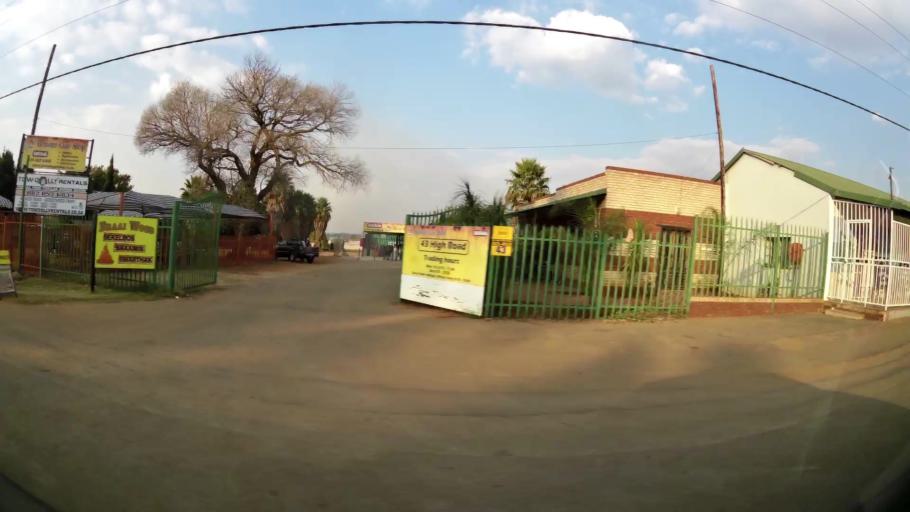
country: ZA
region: Gauteng
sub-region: Ekurhuleni Metropolitan Municipality
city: Benoni
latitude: -26.1237
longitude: 28.2937
